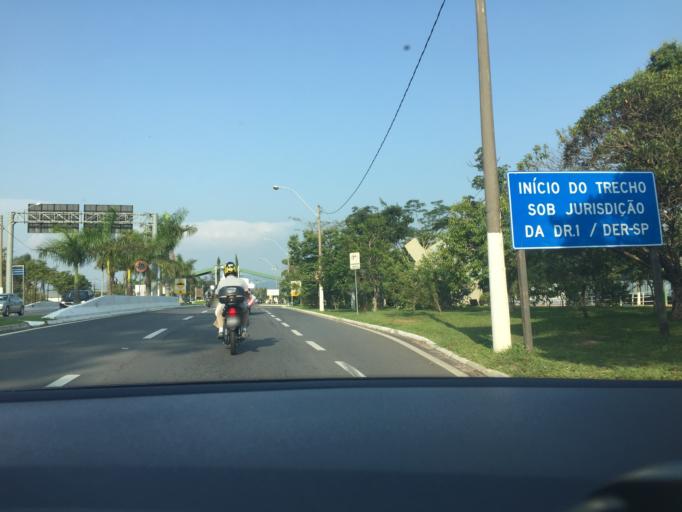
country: BR
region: Sao Paulo
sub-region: Valinhos
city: Valinhos
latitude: -23.0092
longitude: -47.0218
